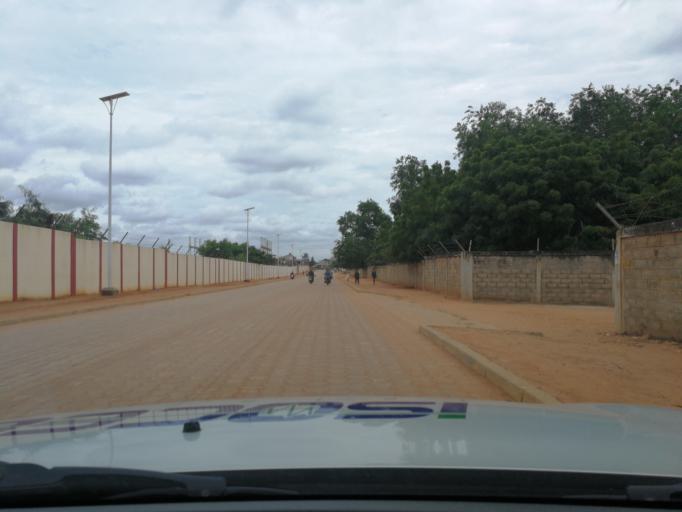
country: BJ
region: Atlantique
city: Hevie
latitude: 6.4271
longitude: 2.3043
